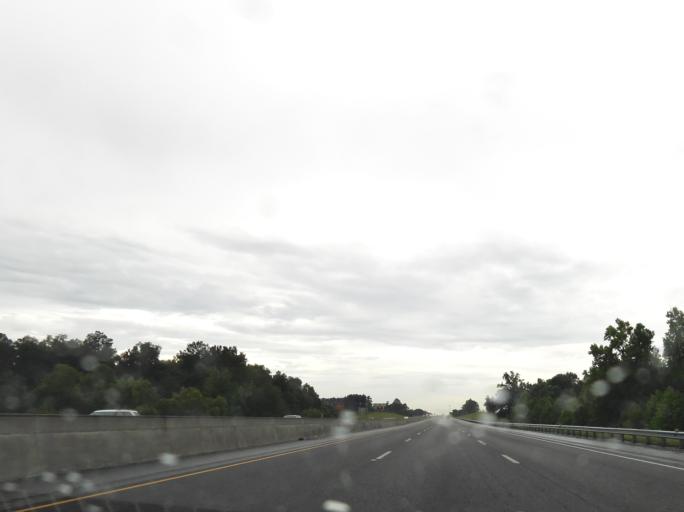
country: US
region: Georgia
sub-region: Lowndes County
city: Hahira
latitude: 30.9699
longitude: -83.3813
